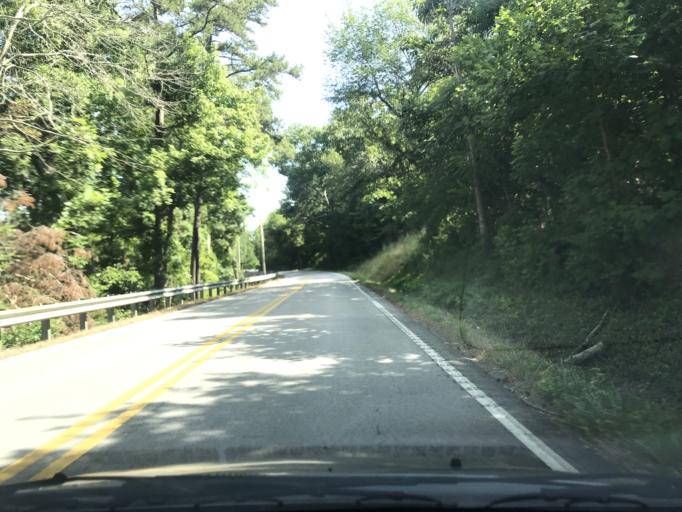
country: US
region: Tennessee
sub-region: Hamilton County
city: Lakesite
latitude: 35.2365
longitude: -85.0711
